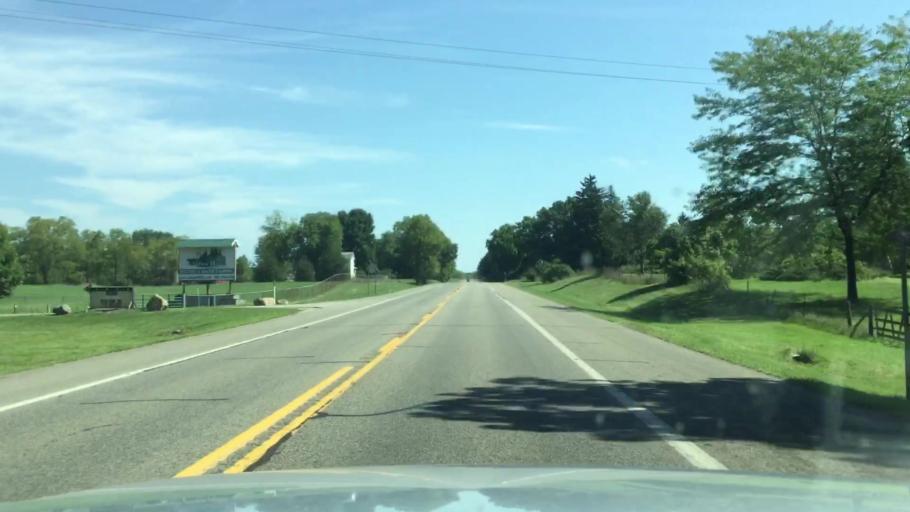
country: US
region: Michigan
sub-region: Jackson County
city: Brooklyn
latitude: 42.0561
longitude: -84.2570
